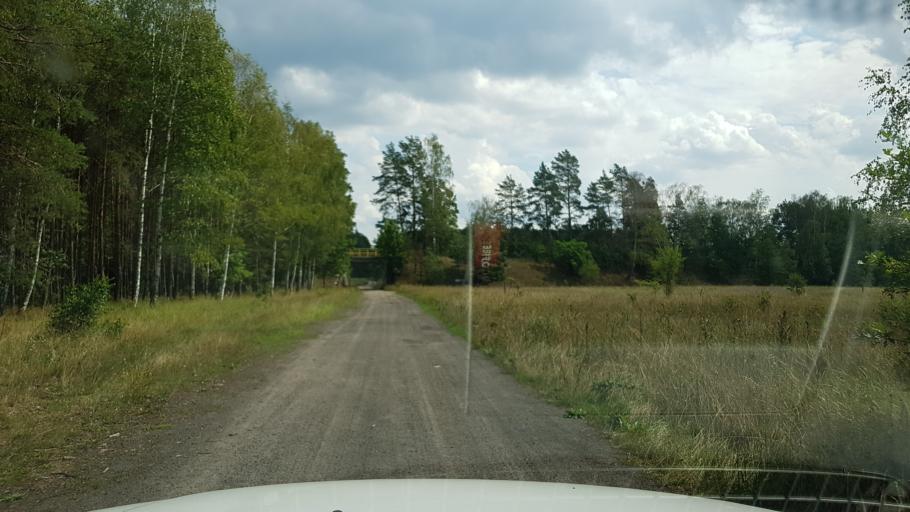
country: PL
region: West Pomeranian Voivodeship
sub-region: Powiat walecki
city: Walcz
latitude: 53.3032
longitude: 16.5343
